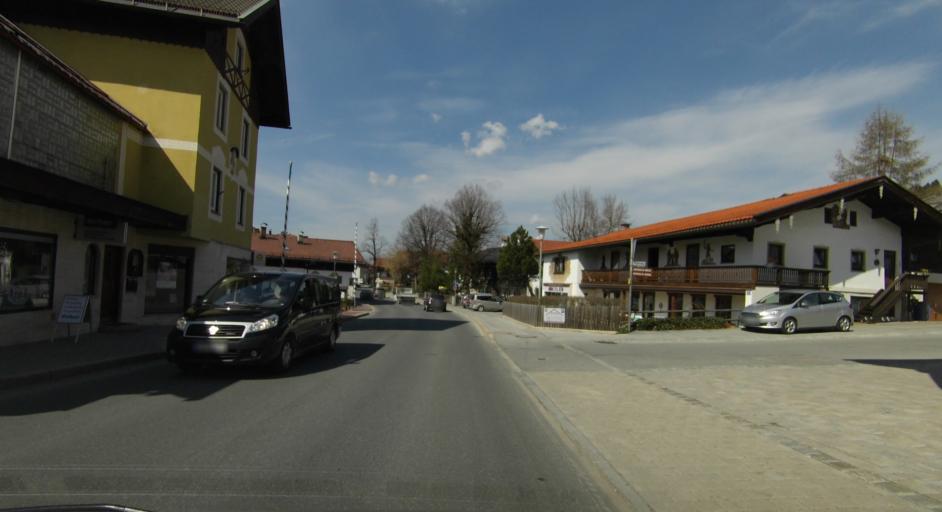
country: DE
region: Bavaria
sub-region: Upper Bavaria
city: Schliersee
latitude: 47.7352
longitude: 11.8633
